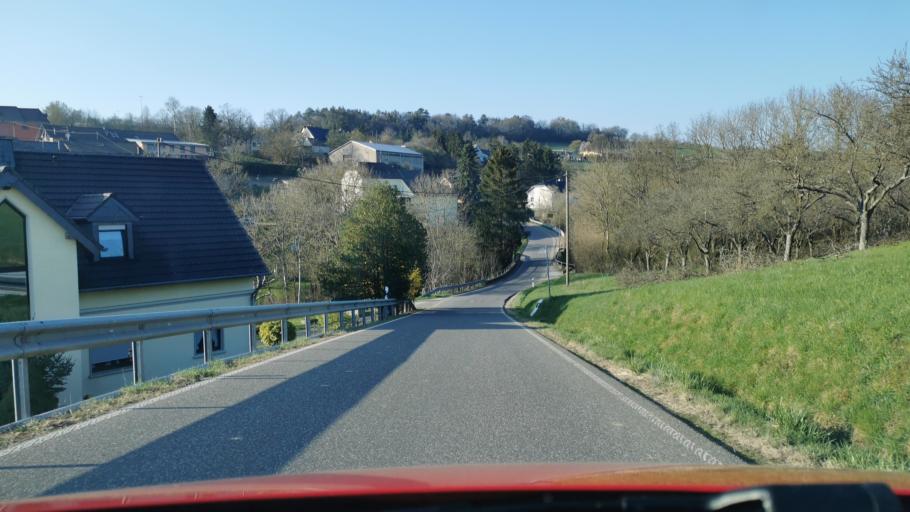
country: DE
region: Rheinland-Pfalz
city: Trierweiler
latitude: 49.7754
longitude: 6.5486
